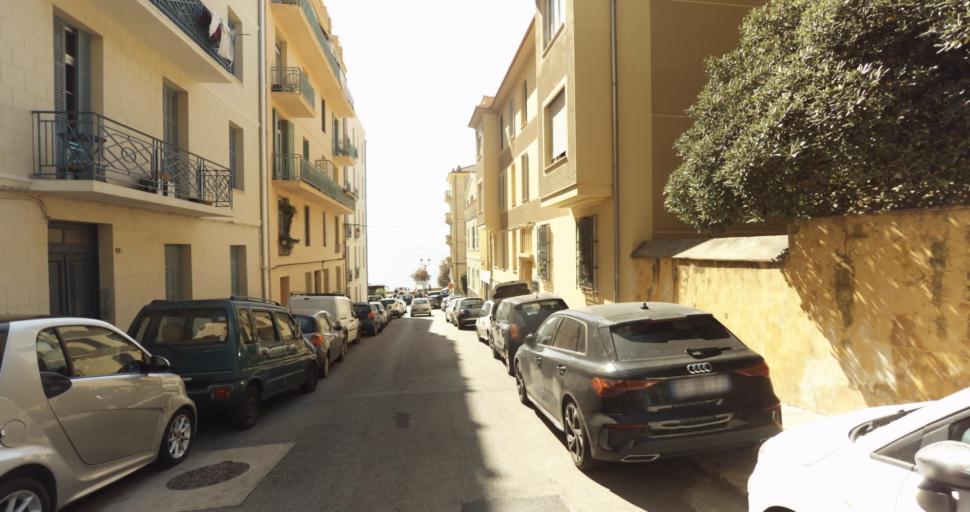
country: FR
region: Corsica
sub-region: Departement de la Corse-du-Sud
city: Ajaccio
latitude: 41.9172
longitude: 8.7313
